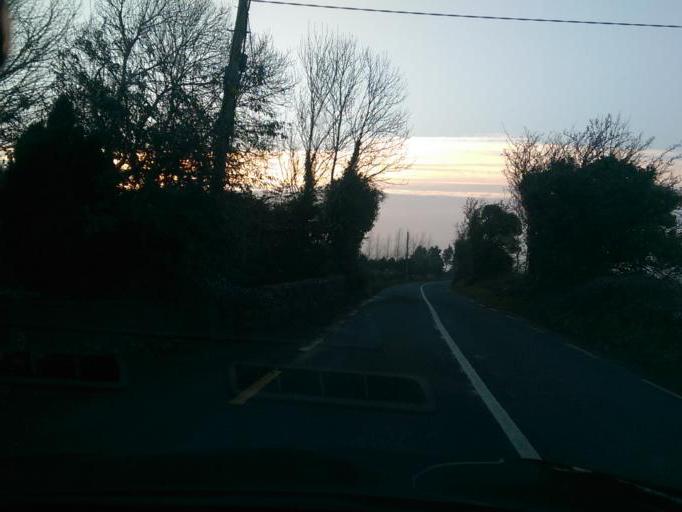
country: IE
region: Connaught
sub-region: County Galway
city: Loughrea
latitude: 53.2139
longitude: -8.6060
